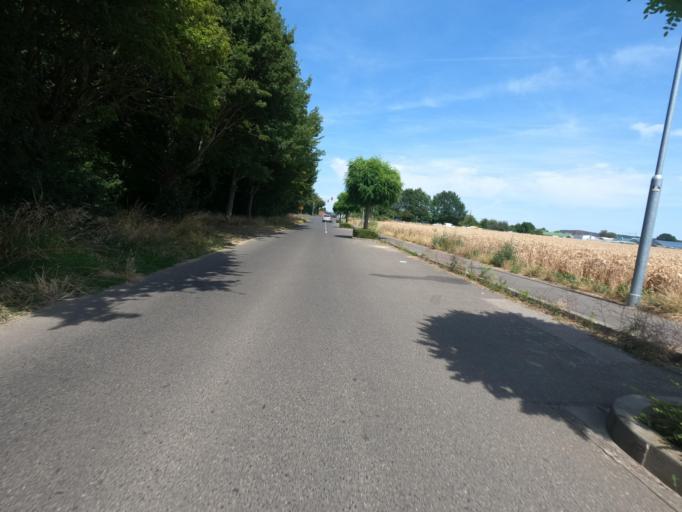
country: DE
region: North Rhine-Westphalia
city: Baesweiler
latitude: 50.9179
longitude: 6.1917
